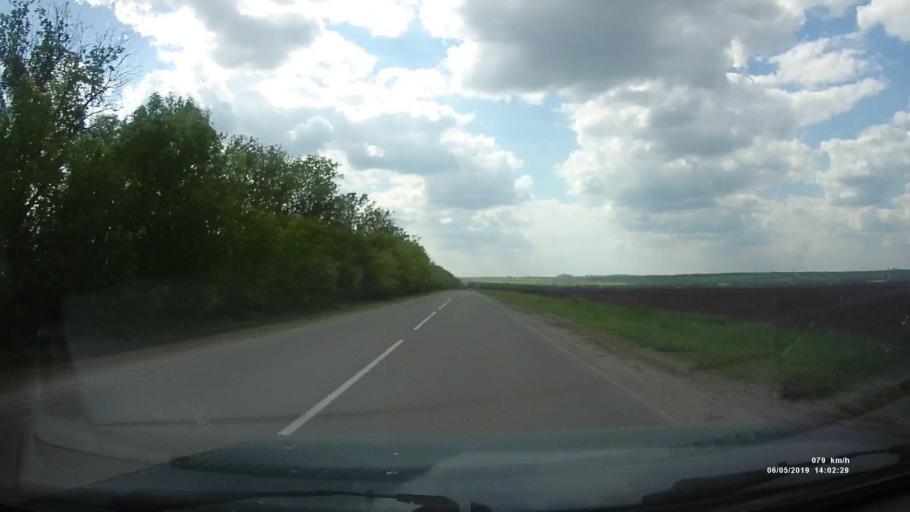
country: RU
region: Rostov
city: Shakhty
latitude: 47.6824
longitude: 40.3628
